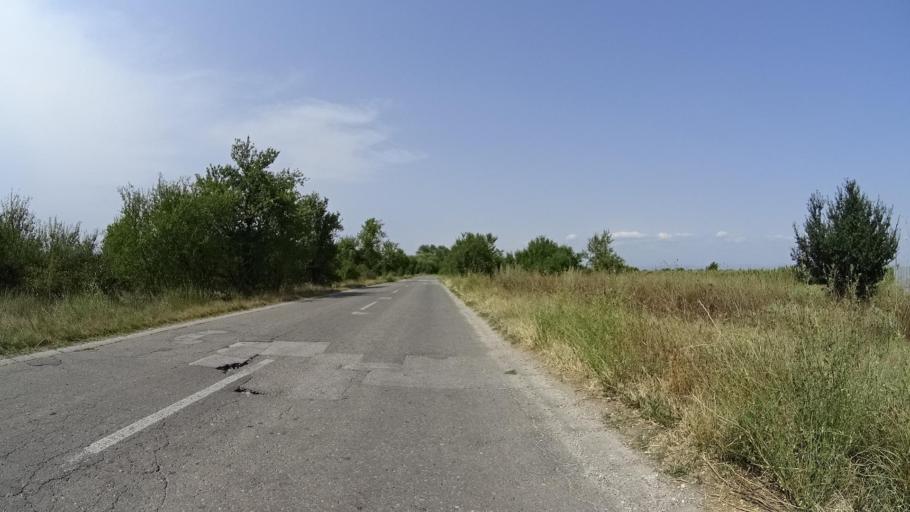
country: BG
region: Plovdiv
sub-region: Obshtina Plovdiv
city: Plovdiv
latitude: 42.2307
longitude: 24.7860
